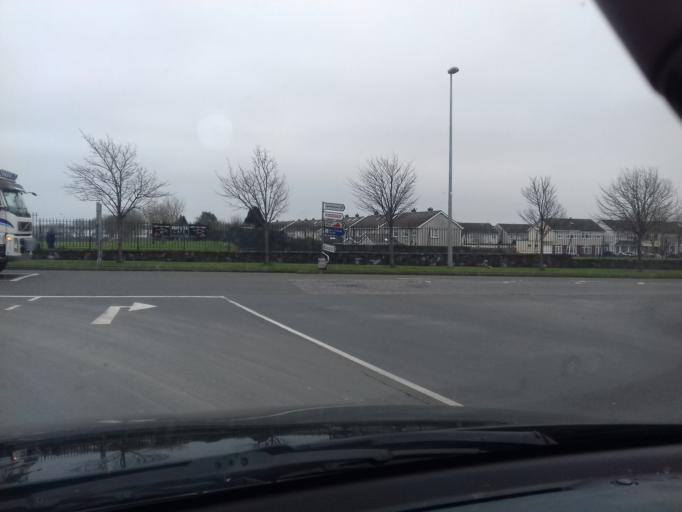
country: IE
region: Leinster
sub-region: Dublin City
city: Finglas
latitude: 53.4012
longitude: -6.3125
